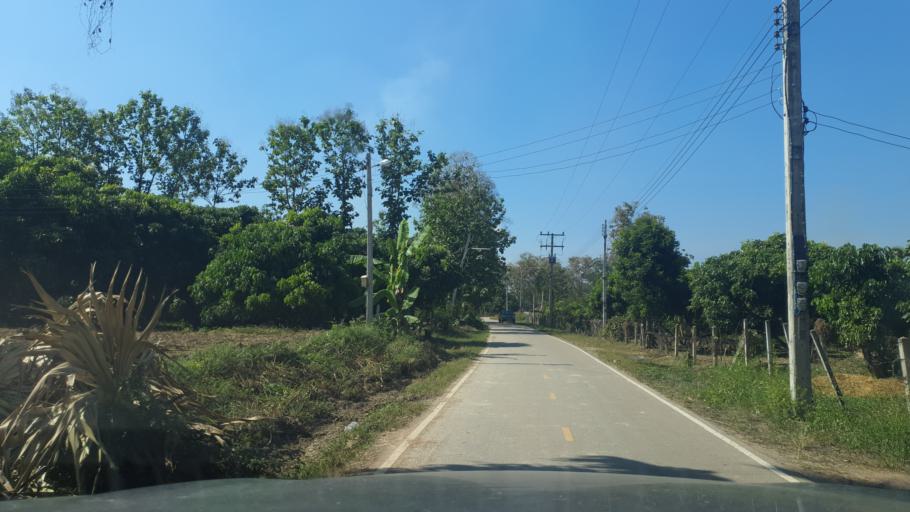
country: TH
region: Chiang Mai
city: Mae On
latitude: 18.7240
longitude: 99.2189
